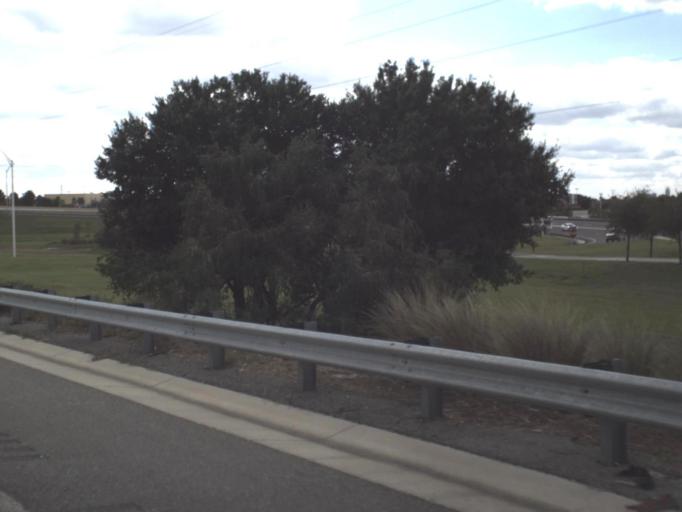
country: US
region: Florida
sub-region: Orange County
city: Tangelo Park
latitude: 28.4764
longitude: -81.4477
